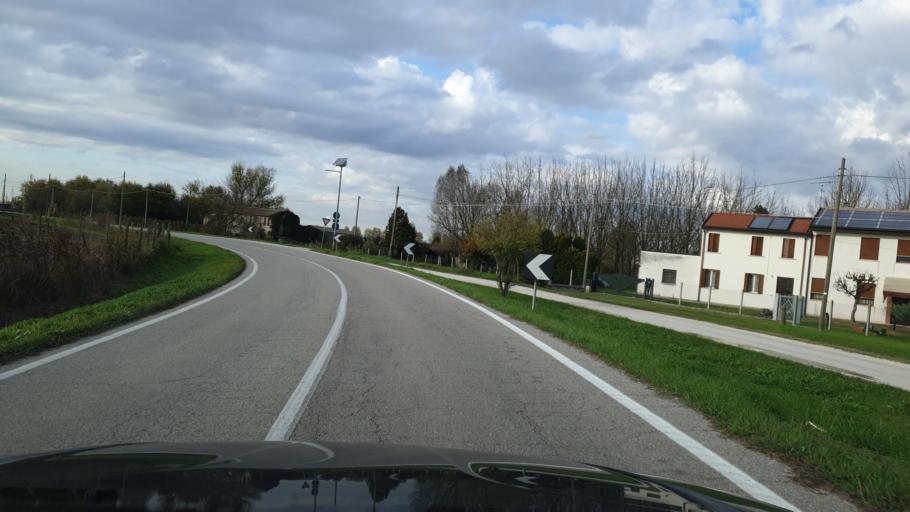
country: IT
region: Veneto
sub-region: Provincia di Rovigo
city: Villanova del Ghebbo Canton
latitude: 45.0687
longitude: 11.6307
